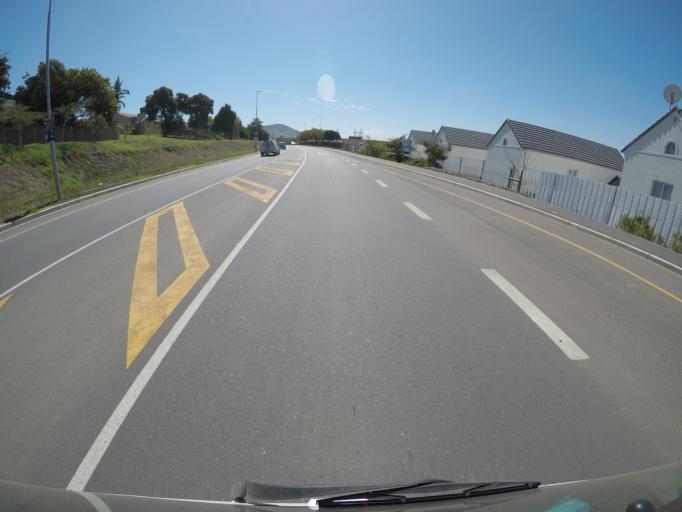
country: ZA
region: Western Cape
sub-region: City of Cape Town
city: Kraaifontein
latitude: -33.8245
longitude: 18.6370
